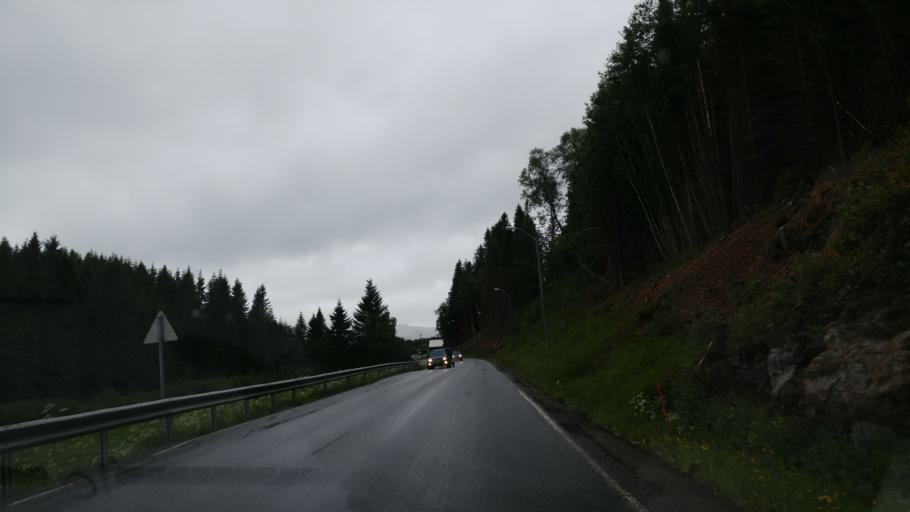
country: NO
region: Sor-Trondelag
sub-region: Selbu
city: Mebonden
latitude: 63.2565
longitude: 11.0846
